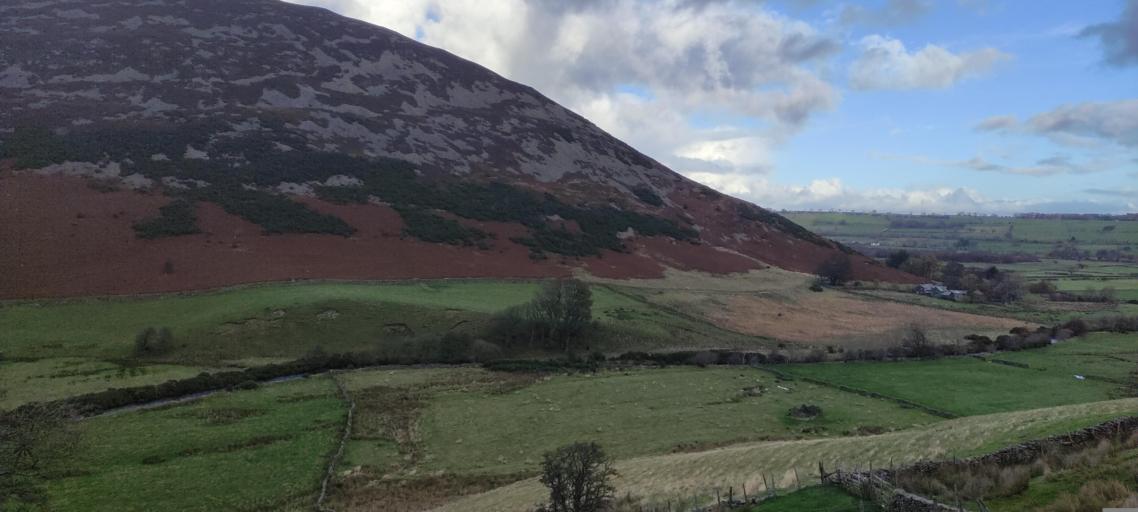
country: GB
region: England
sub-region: Cumbria
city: Keswick
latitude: 54.6769
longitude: -3.0092
